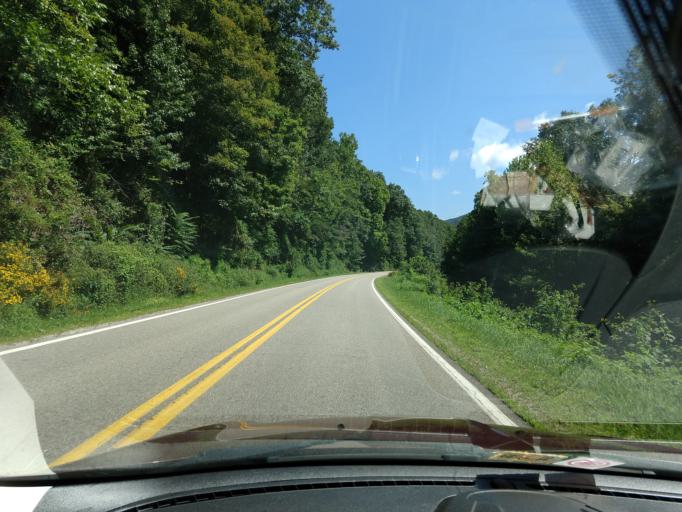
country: US
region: West Virginia
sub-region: Kanawha County
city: Montgomery
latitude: 38.1356
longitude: -81.2188
